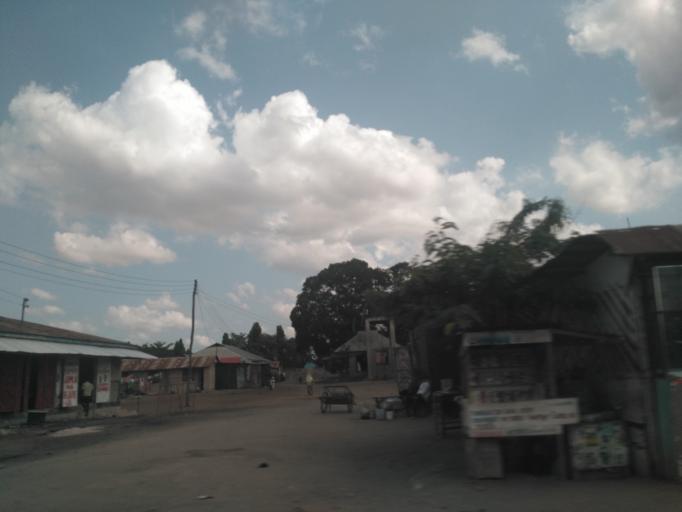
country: TZ
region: Dar es Salaam
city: Dar es Salaam
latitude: -6.8964
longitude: 39.2702
